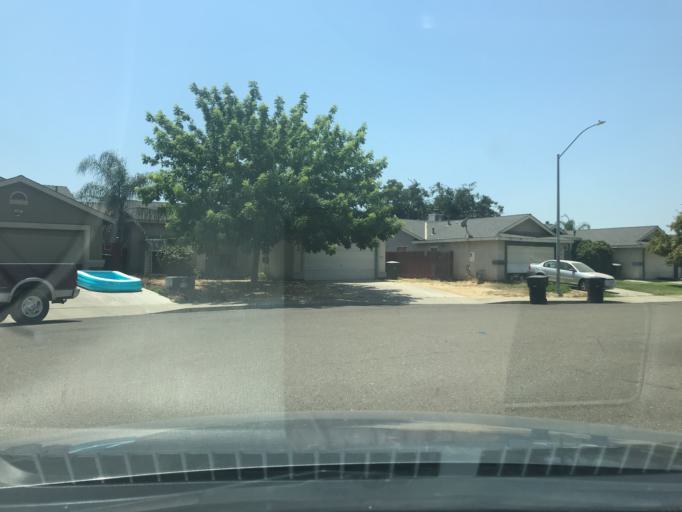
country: US
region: California
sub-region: Merced County
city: Atwater
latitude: 37.3625
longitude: -120.5972
